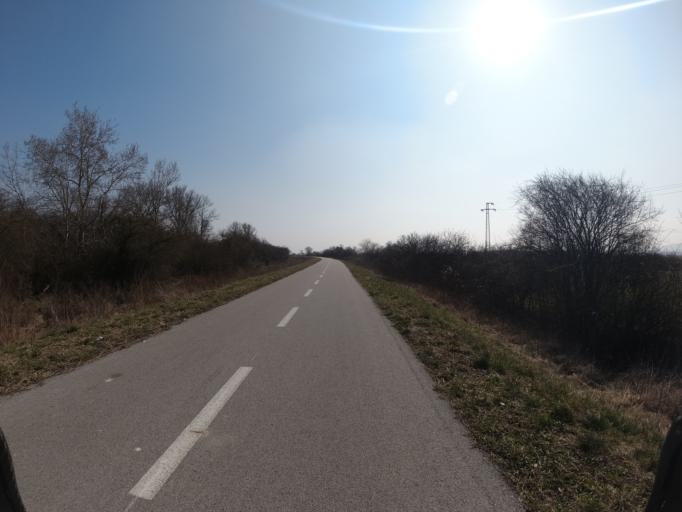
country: SK
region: Trenciansky
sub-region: Okres Nove Mesto nad Vahom
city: Nove Mesto nad Vahom
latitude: 48.7398
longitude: 17.8468
